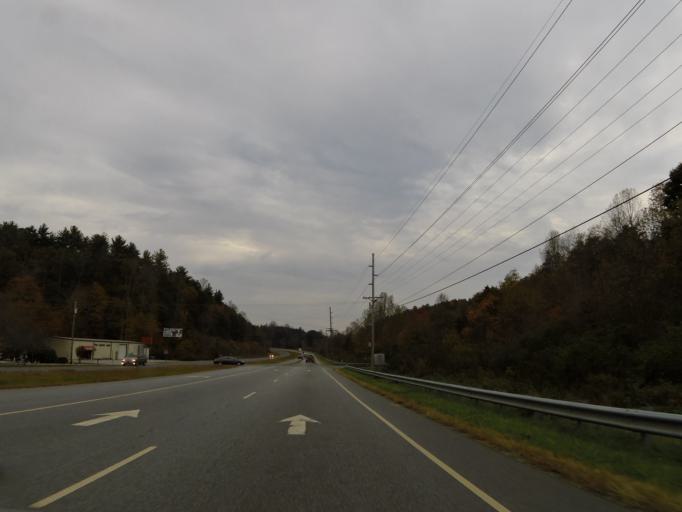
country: US
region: North Carolina
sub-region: Caldwell County
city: Lenoir
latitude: 35.9449
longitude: -81.5467
